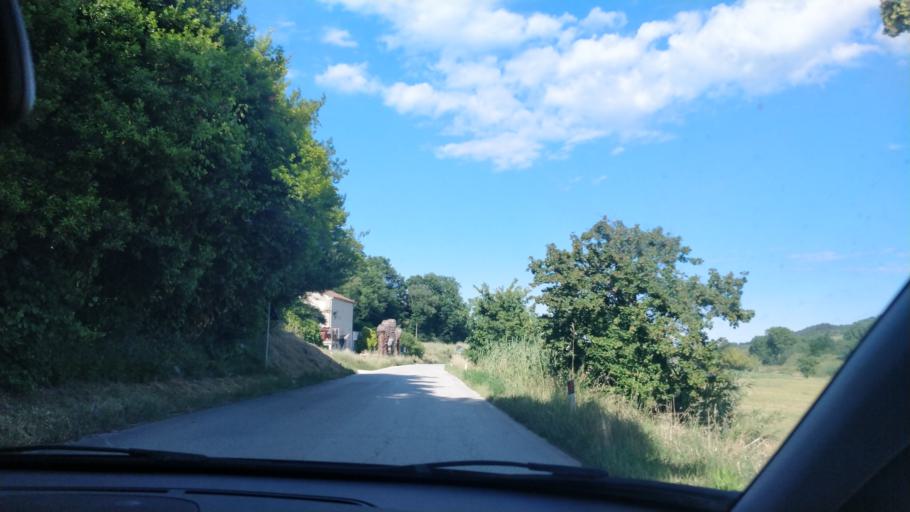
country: IT
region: The Marches
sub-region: Provincia di Ascoli Piceno
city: Massignano
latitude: 43.0374
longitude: 13.8065
